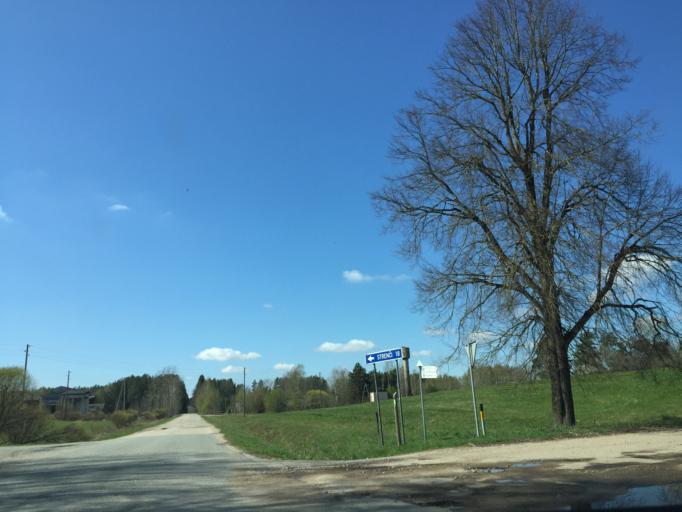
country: LV
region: Smiltene
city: Smiltene
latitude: 57.5866
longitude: 25.9478
